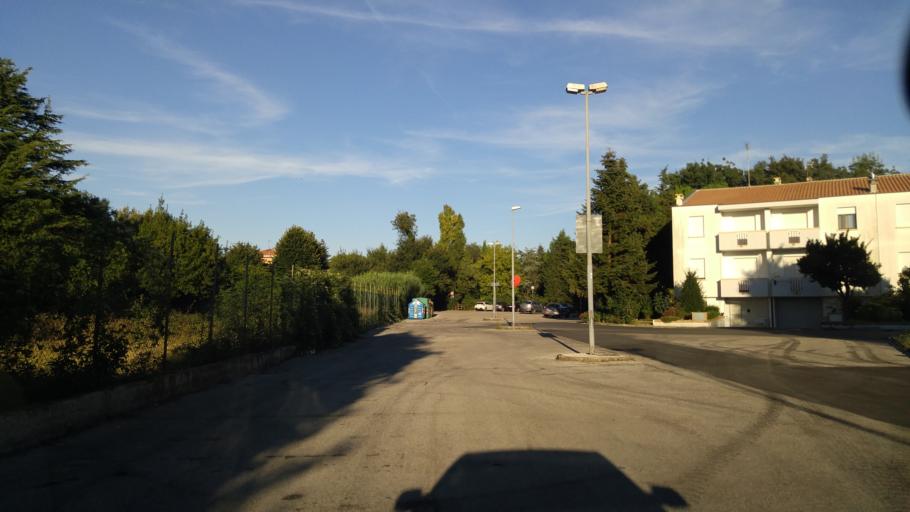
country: IT
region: The Marches
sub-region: Provincia di Pesaro e Urbino
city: Fano
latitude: 43.8334
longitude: 13.0205
